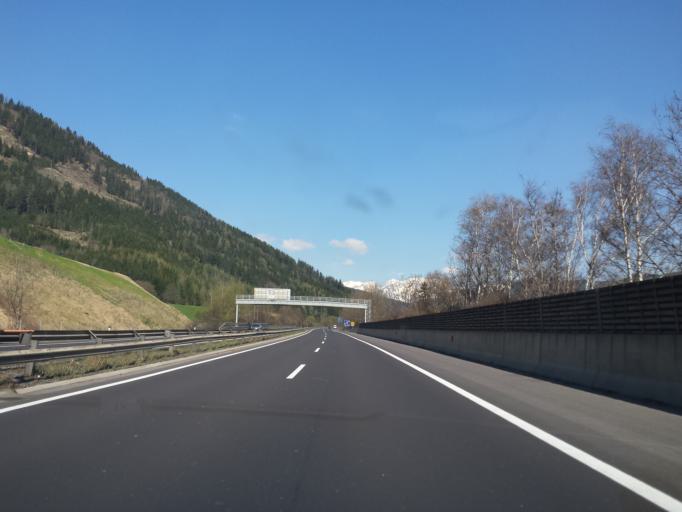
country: AT
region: Styria
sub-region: Politischer Bezirk Leoben
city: Sankt Michael in Obersteiermark
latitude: 47.3504
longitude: 15.0055
